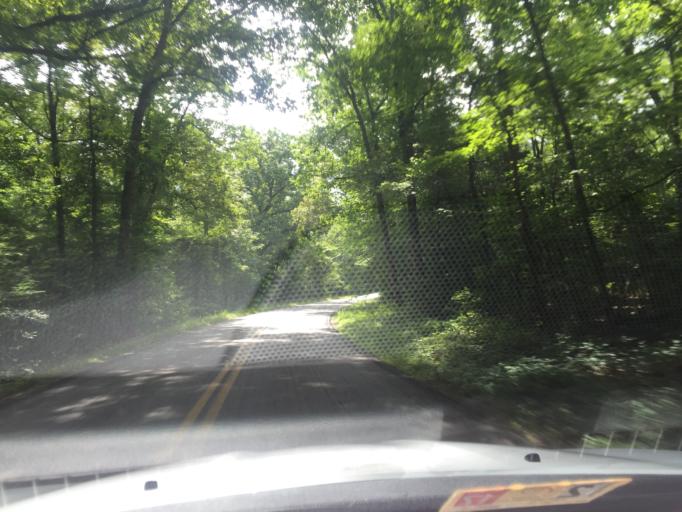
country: US
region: Virginia
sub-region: Charles City County
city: Charles City
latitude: 37.4105
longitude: -77.0307
